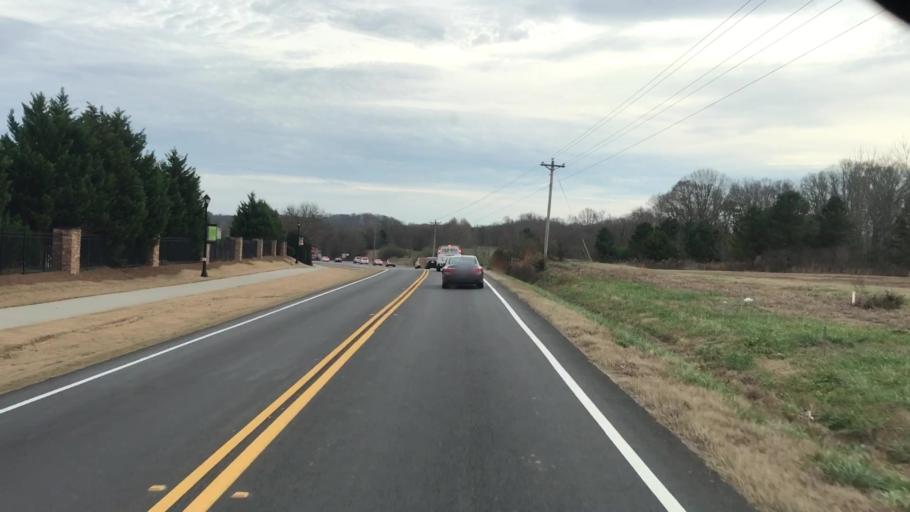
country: US
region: Georgia
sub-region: Jackson County
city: Braselton
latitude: 34.1180
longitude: -83.8249
